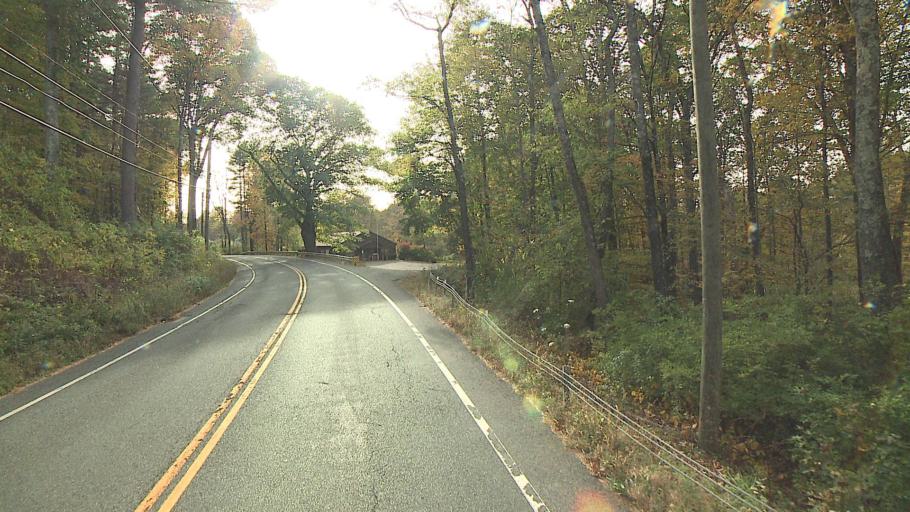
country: US
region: Connecticut
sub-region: Litchfield County
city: Canaan
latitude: 42.0154
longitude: -73.3517
